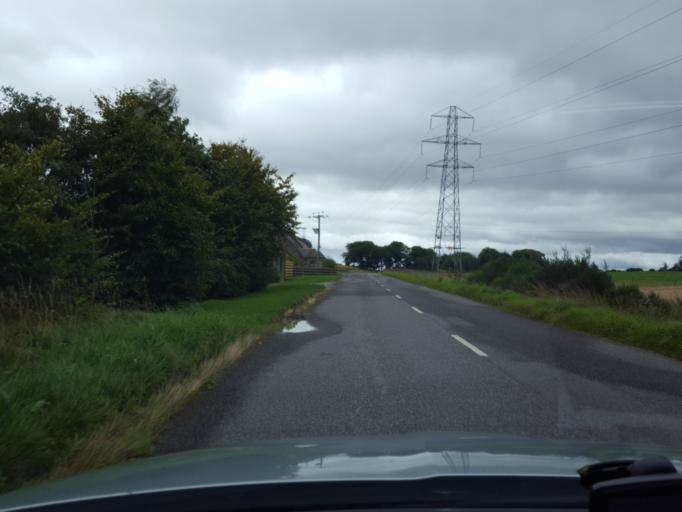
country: GB
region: Scotland
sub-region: Aberdeenshire
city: Banchory
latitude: 57.1476
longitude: -2.5095
